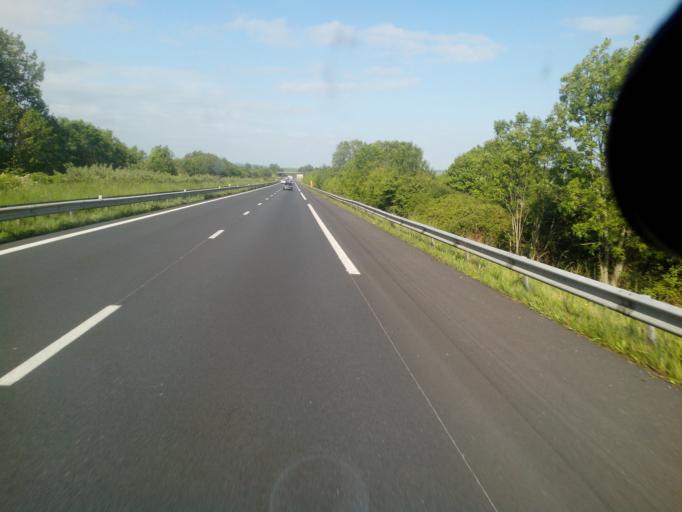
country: FR
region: Lower Normandy
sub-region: Departement du Calvados
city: Dives-sur-Mer
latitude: 49.2185
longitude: -0.1212
